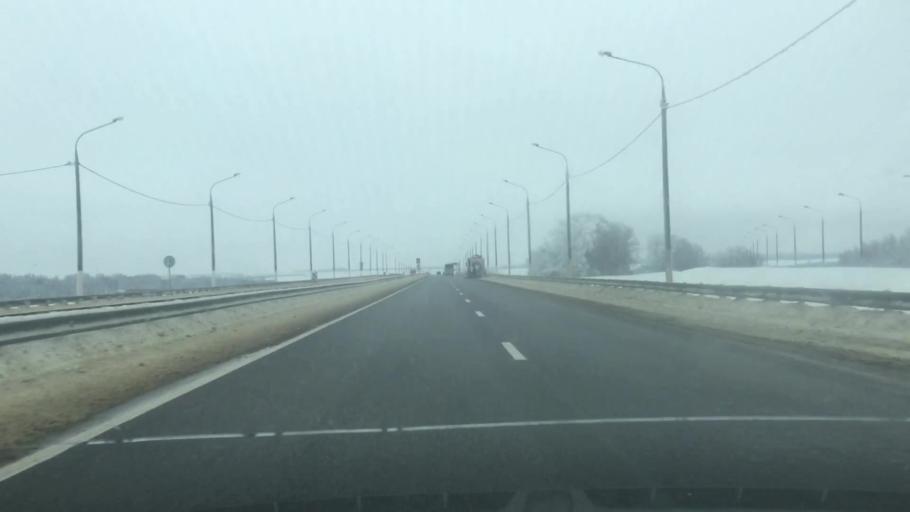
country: RU
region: Tula
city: Kazachka
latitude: 53.2918
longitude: 38.1783
